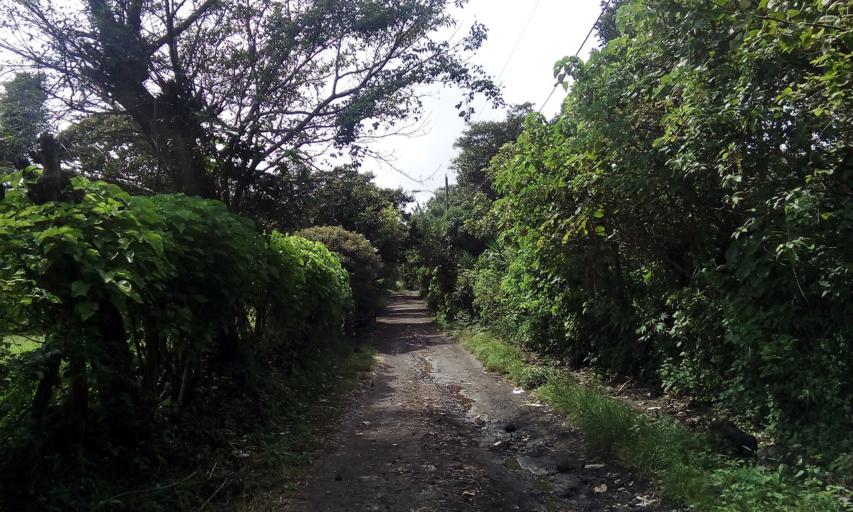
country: GT
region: Escuintla
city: San Vicente Pacaya
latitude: 14.3343
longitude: -90.6040
